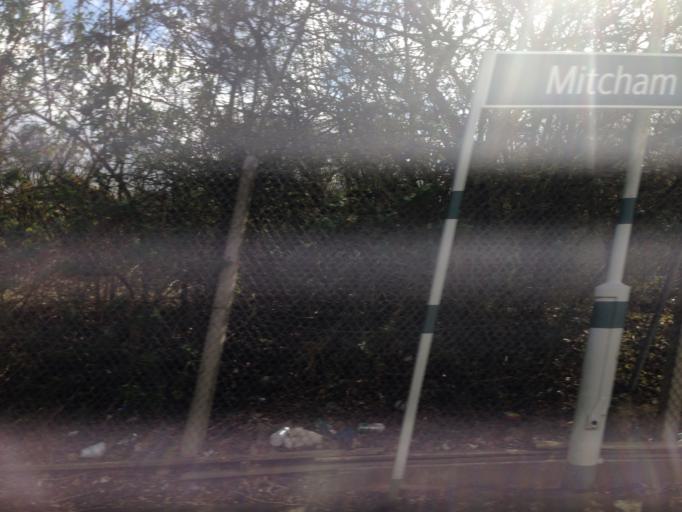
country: GB
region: England
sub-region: Greater London
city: Mitcham
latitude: 51.3926
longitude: -0.1567
